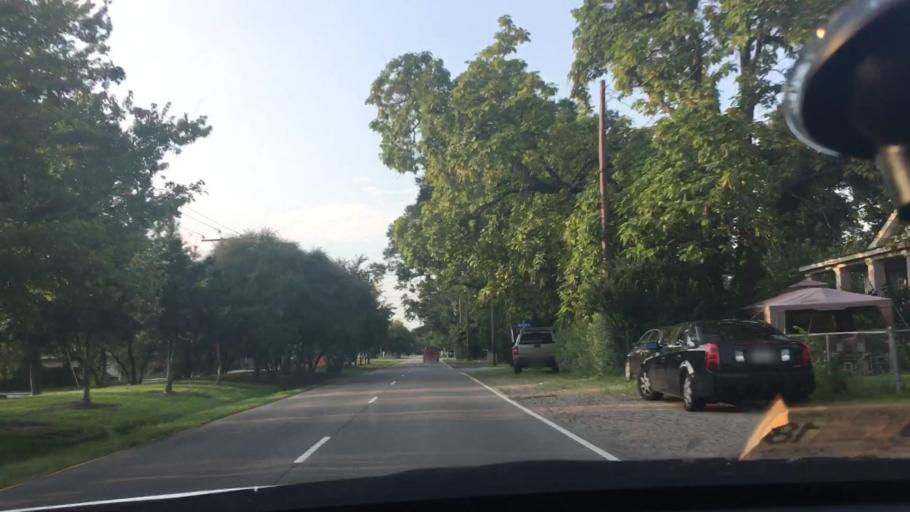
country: US
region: Virginia
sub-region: City of Norfolk
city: Norfolk
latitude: 36.9377
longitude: -76.2449
